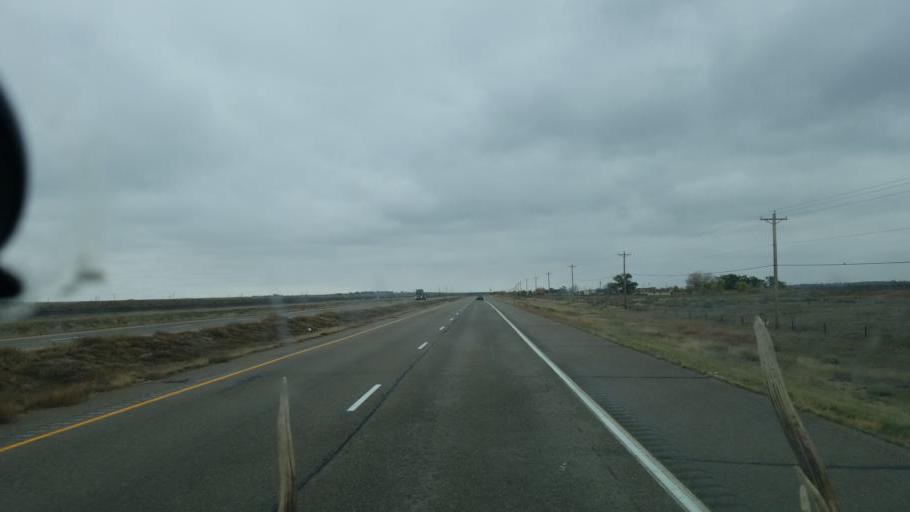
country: US
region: Colorado
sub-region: Pueblo County
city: Pueblo
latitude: 38.2708
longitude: -104.4159
